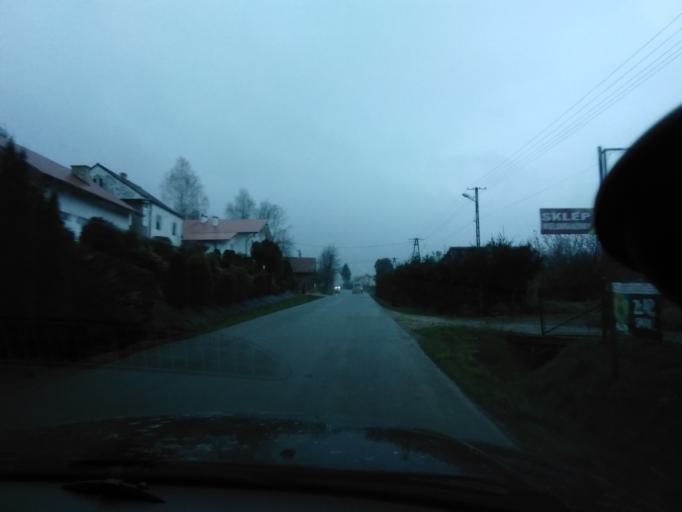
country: PL
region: Subcarpathian Voivodeship
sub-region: Powiat brzozowski
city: Wesola
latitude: 49.7492
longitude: 22.1205
